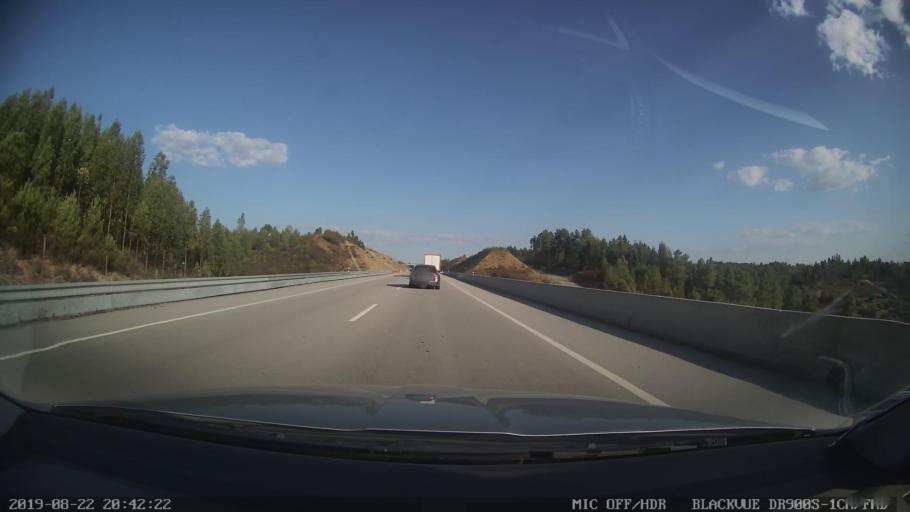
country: PT
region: Castelo Branco
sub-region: Proenca-A-Nova
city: Proenca-a-Nova
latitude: 39.6940
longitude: -7.8159
